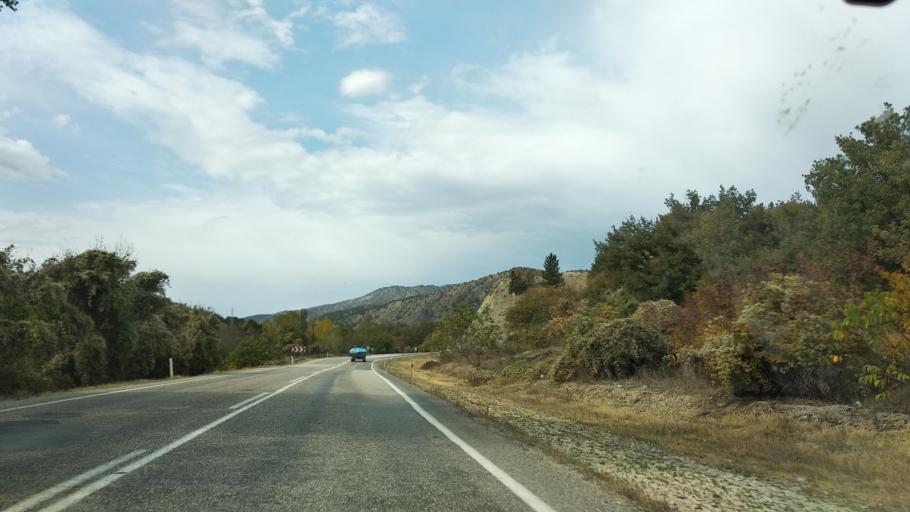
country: TR
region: Ankara
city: Nallihan
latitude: 40.3085
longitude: 31.2732
